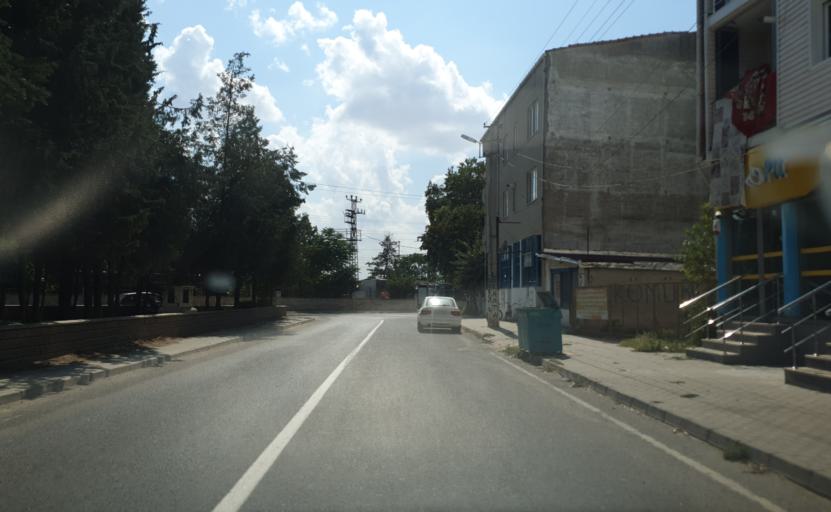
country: TR
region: Kirklareli
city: Luleburgaz
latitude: 41.3562
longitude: 27.3337
